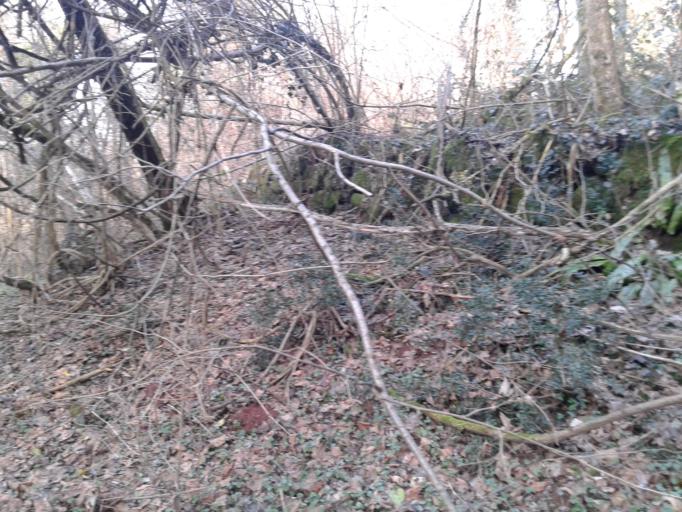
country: IT
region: Veneto
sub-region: Provincia di Vicenza
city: Monte di Malo
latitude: 45.6677
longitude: 11.3661
